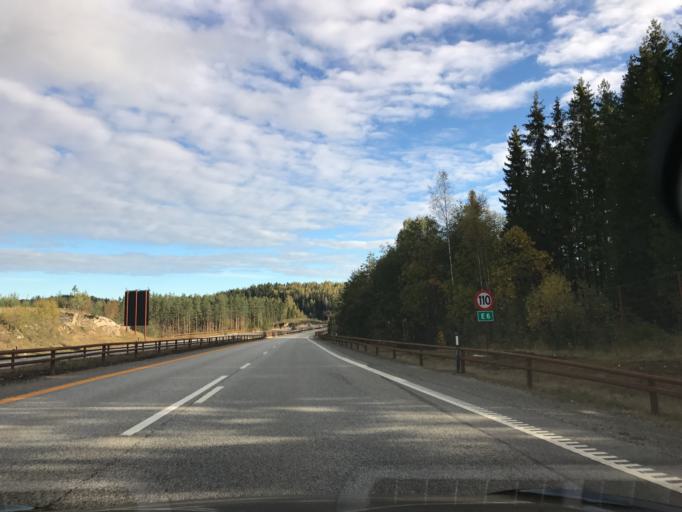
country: NO
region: Akershus
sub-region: Eidsvoll
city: Raholt
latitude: 60.3163
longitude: 11.1500
